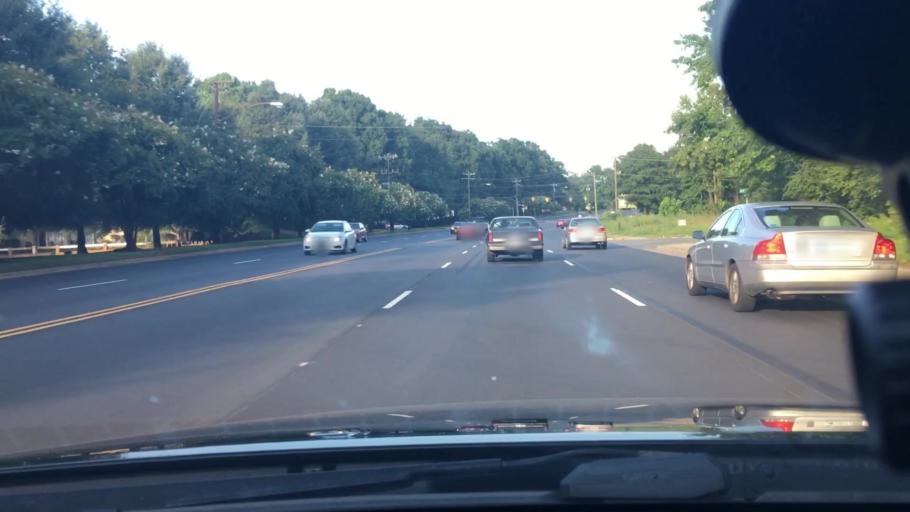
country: US
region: North Carolina
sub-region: Mecklenburg County
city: Charlotte
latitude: 35.2032
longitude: -80.7560
